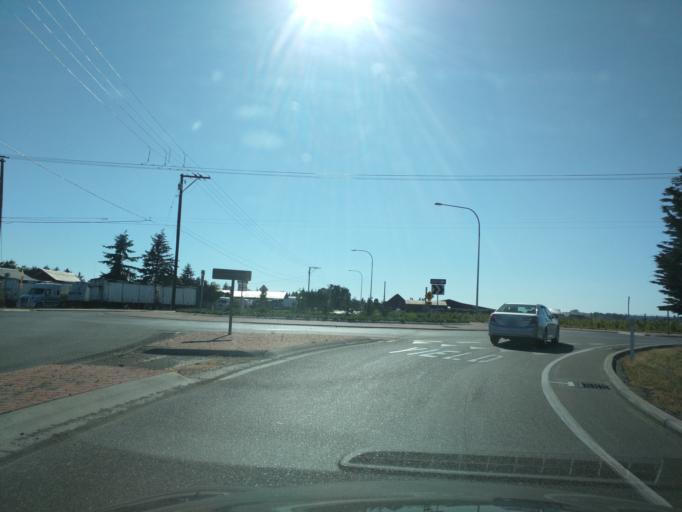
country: US
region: Washington
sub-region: Whatcom County
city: Lynden
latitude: 48.9644
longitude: -122.4406
